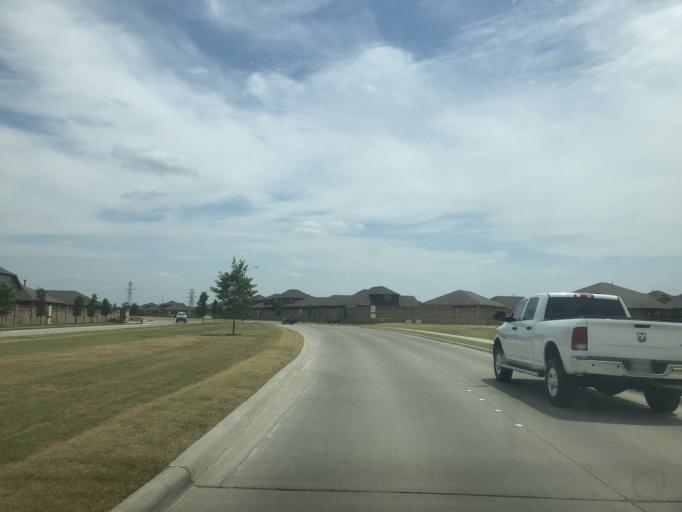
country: US
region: Texas
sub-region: Tarrant County
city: Saginaw
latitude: 32.8802
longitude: -97.3553
